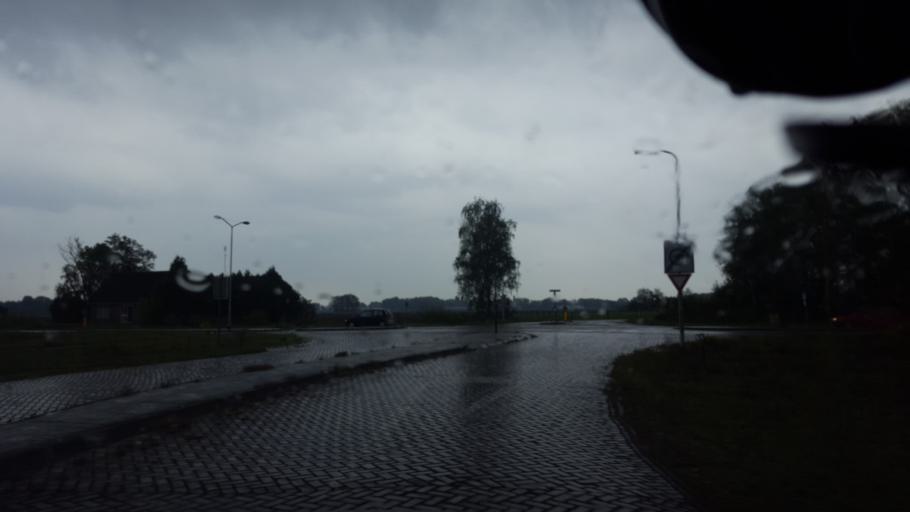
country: NL
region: North Brabant
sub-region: Gemeente Someren
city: Someren
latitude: 51.3871
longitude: 5.6681
